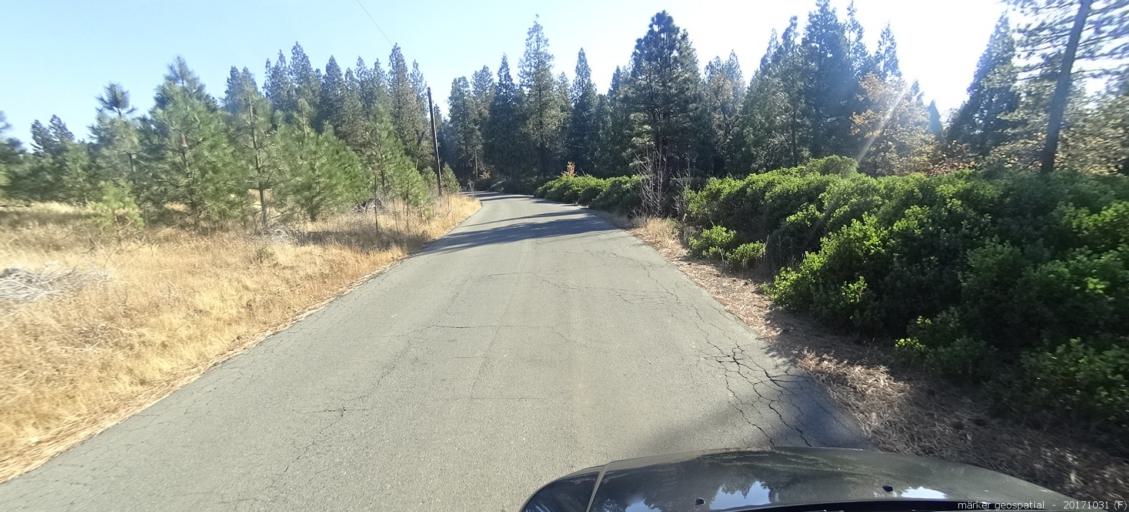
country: US
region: California
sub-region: Shasta County
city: Shingletown
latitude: 40.5176
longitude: -121.8205
